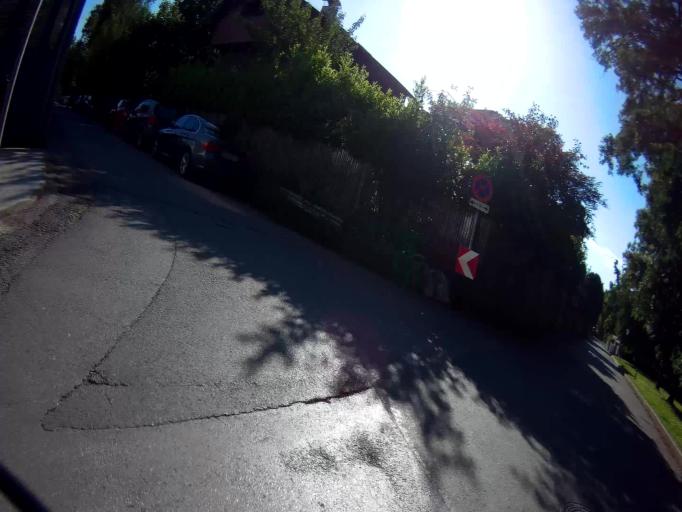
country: AT
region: Salzburg
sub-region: Salzburg Stadt
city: Salzburg
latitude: 47.7958
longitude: 13.0634
